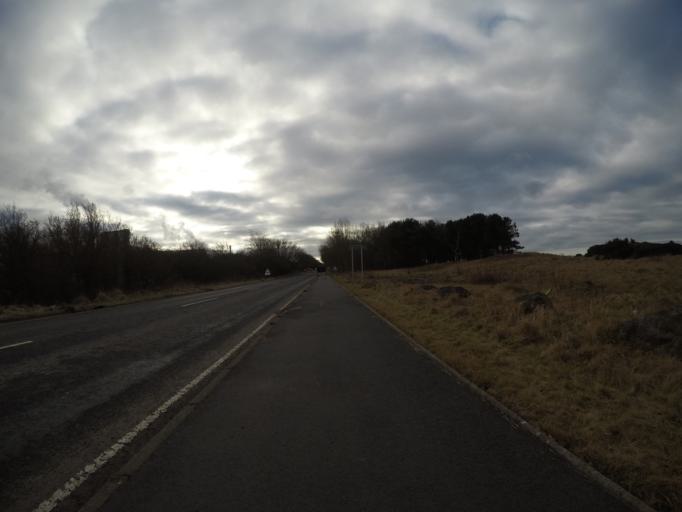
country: GB
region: Scotland
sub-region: North Ayrshire
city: Irvine
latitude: 55.5866
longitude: -4.6480
